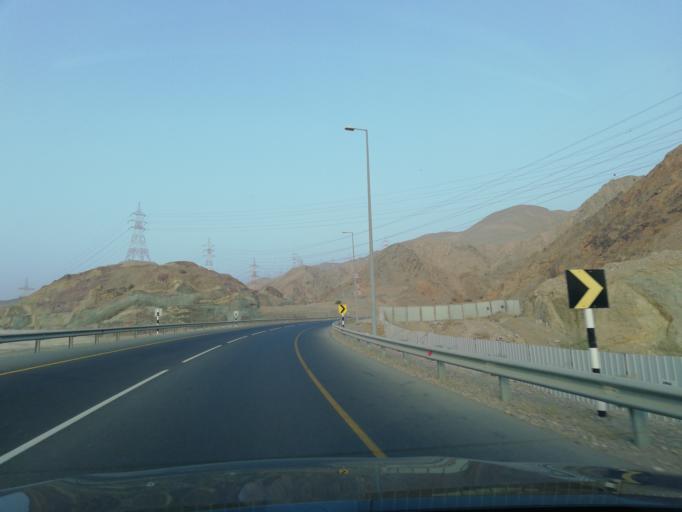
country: OM
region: Muhafazat Masqat
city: Bawshar
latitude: 23.5792
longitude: 58.4424
